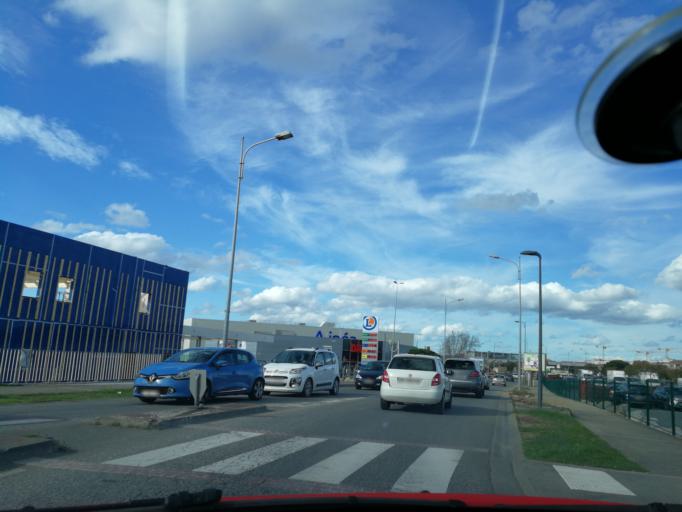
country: FR
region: Midi-Pyrenees
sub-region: Departement de la Haute-Garonne
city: Beauzelle
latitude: 43.6464
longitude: 1.3687
